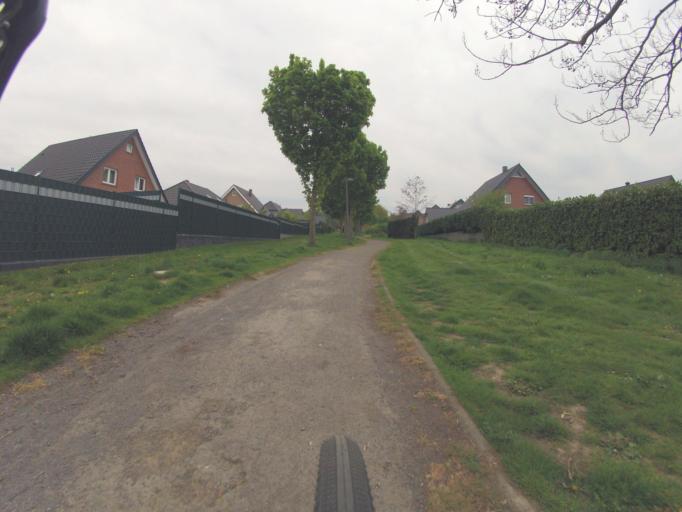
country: DE
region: North Rhine-Westphalia
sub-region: Regierungsbezirk Munster
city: Mettingen
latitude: 52.3107
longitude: 7.7897
